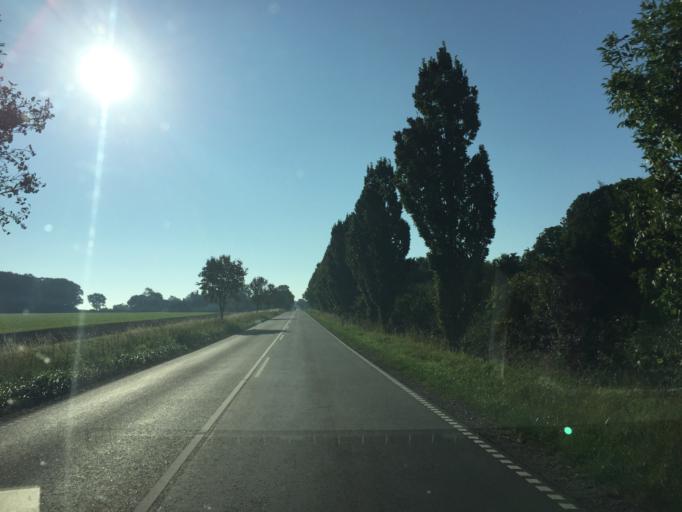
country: DK
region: South Denmark
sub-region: Kerteminde Kommune
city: Kerteminde
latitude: 55.4099
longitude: 10.7167
